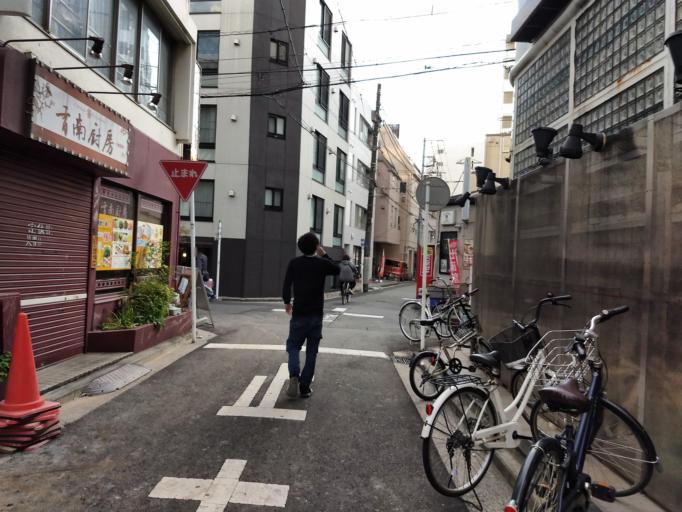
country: JP
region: Kanagawa
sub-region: Kawasaki-shi
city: Kawasaki
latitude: 35.5067
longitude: 139.6789
